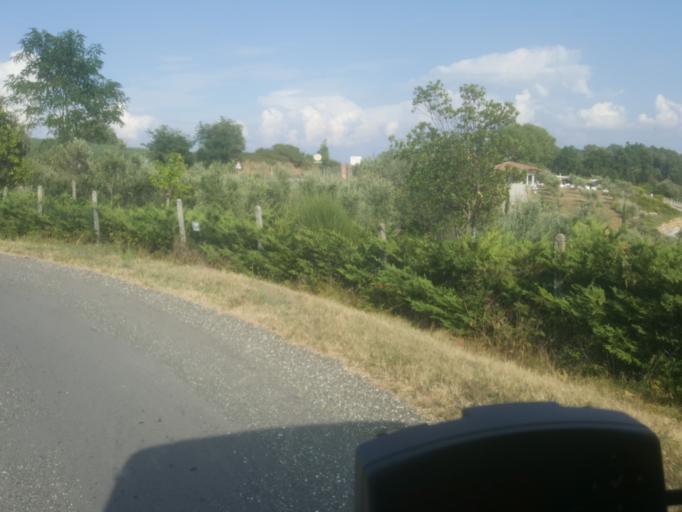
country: IT
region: Tuscany
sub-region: Province of Florence
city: Gambassi Terme
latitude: 43.4897
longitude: 10.9324
